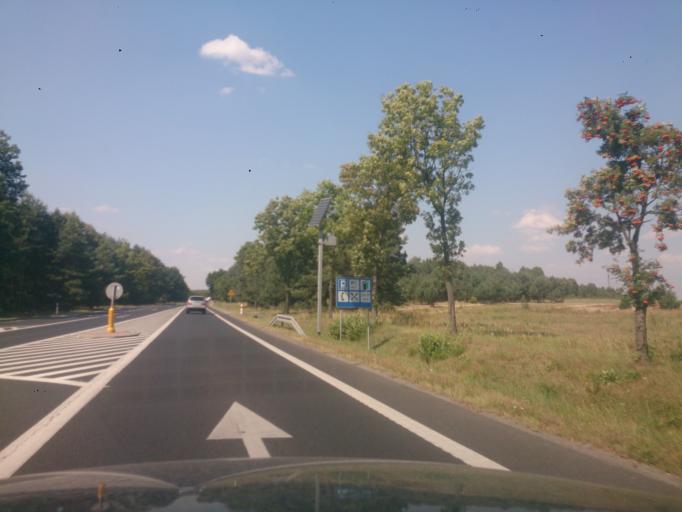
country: PL
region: Subcarpathian Voivodeship
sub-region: Powiat rzeszowski
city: Glogow Malopolski
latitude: 50.1910
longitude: 21.8928
